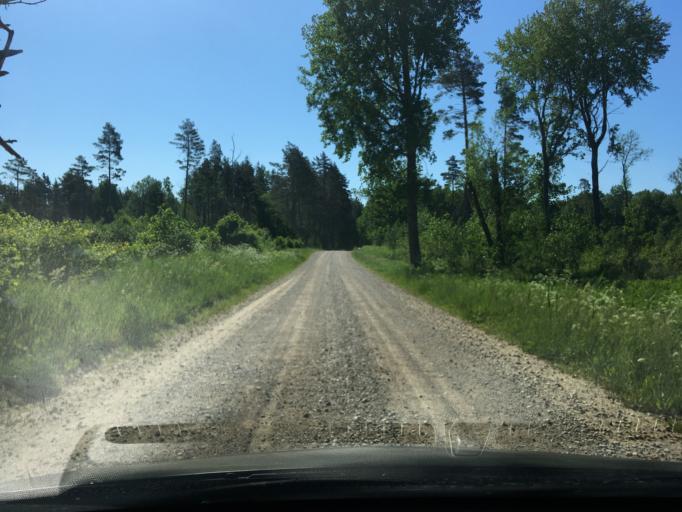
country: EE
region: Laeaene
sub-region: Lihula vald
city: Lihula
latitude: 58.6450
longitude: 23.7847
